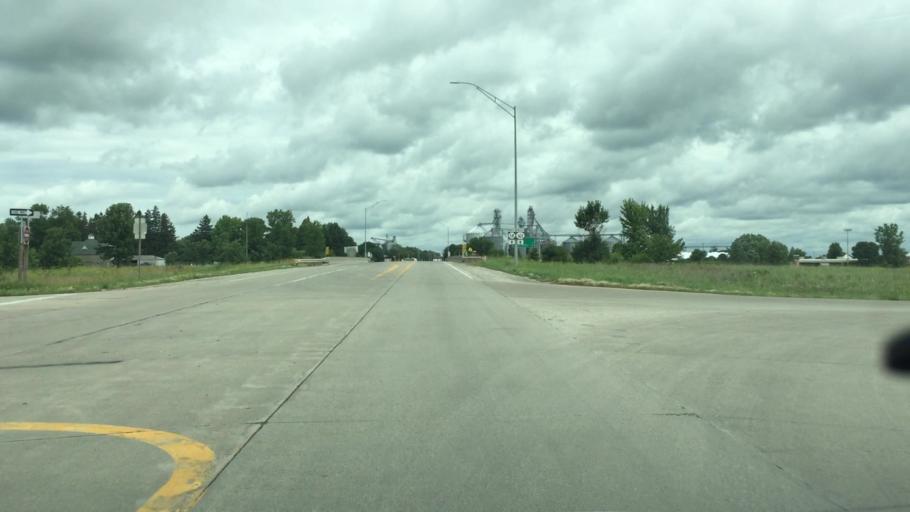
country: US
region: Iowa
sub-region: Jasper County
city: Monroe
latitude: 41.5101
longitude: -93.1011
